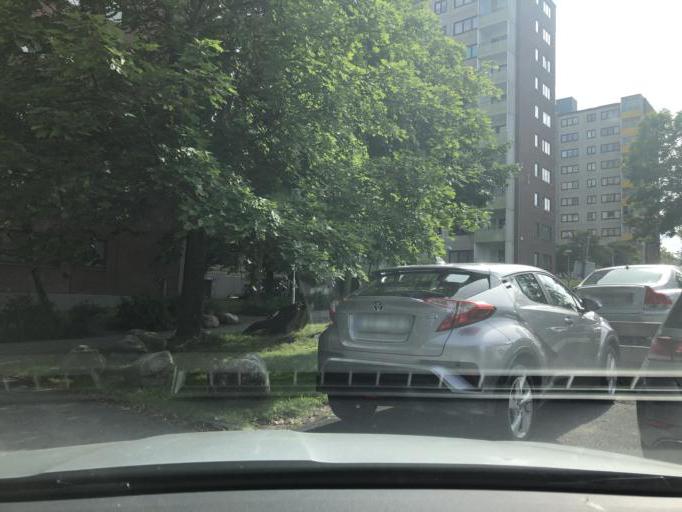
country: SE
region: Stockholm
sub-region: Botkyrka Kommun
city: Fittja
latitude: 59.2487
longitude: 17.8656
